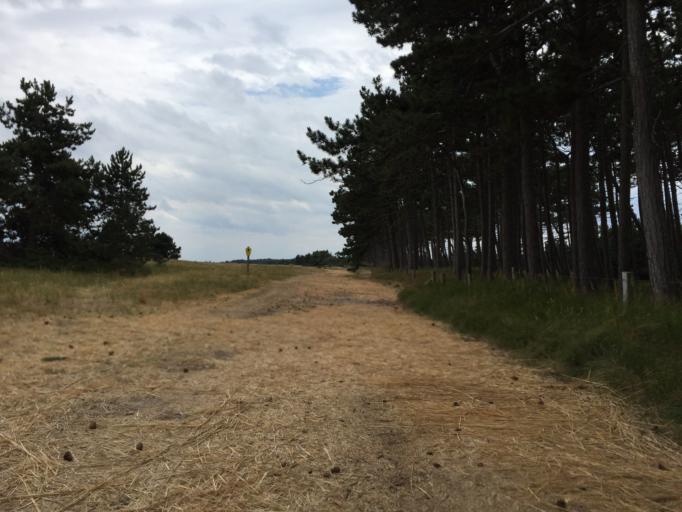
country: DE
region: Mecklenburg-Vorpommern
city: Hiddensee
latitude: 54.5103
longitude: 13.0762
